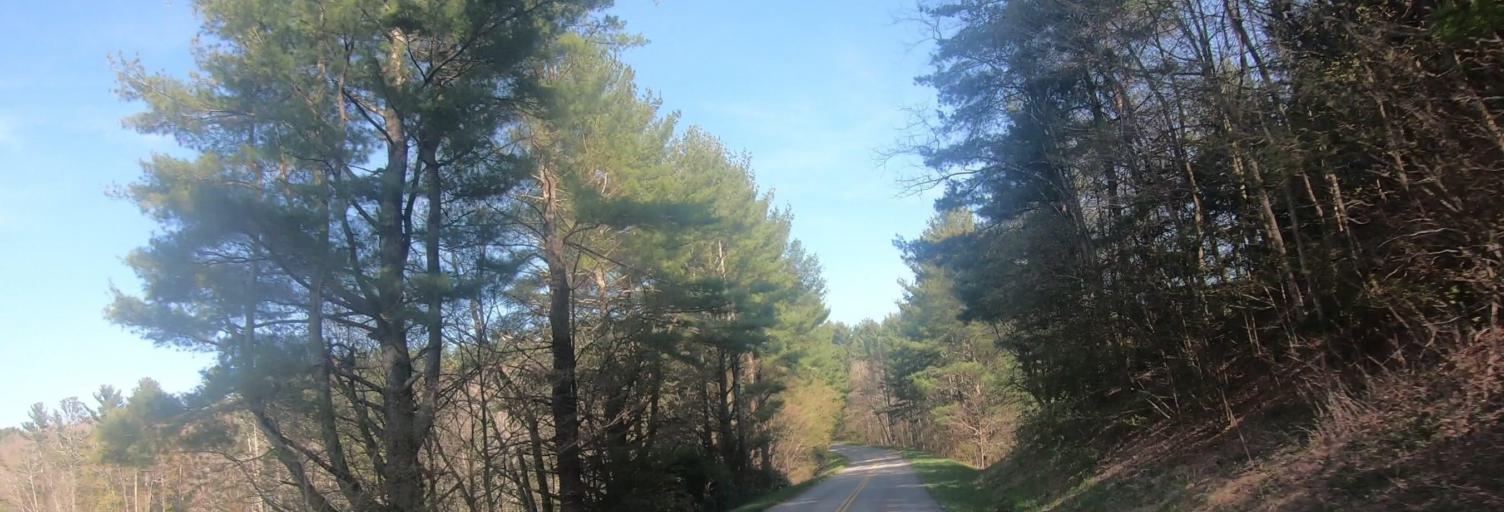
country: US
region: North Carolina
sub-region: Watauga County
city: Boone
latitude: 36.2301
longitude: -81.5458
